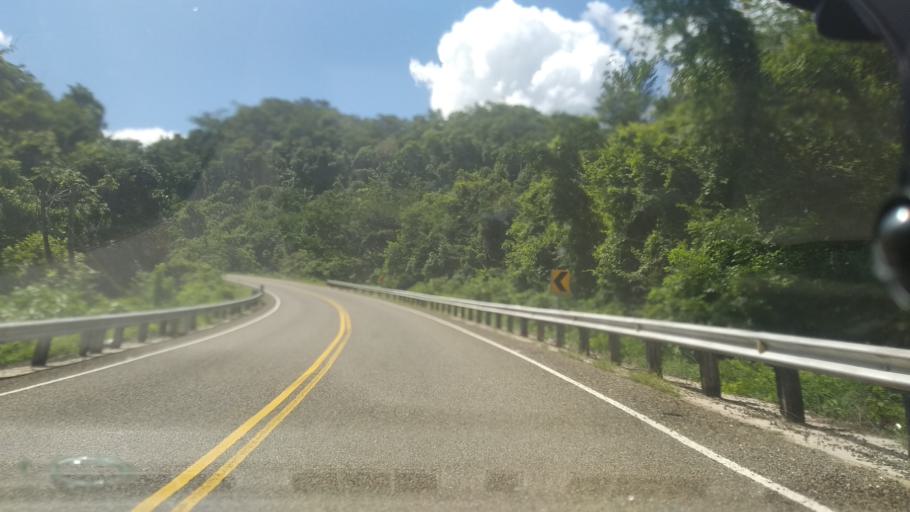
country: BZ
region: Cayo
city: Belmopan
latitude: 17.1504
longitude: -88.6612
